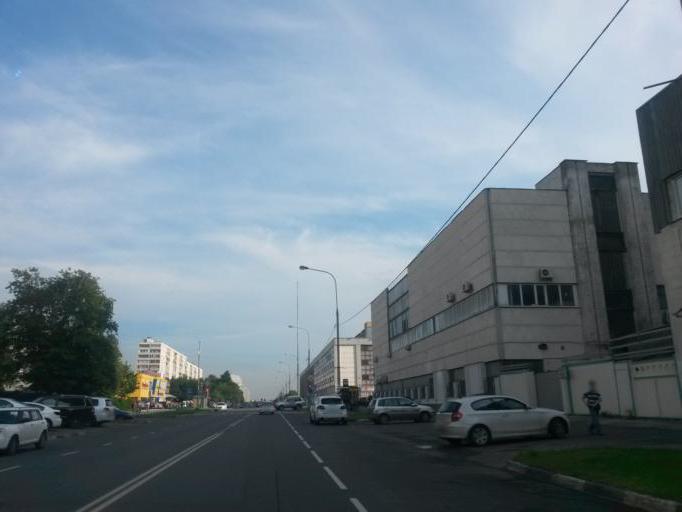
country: RU
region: Moscow
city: Orekhovo-Borisovo
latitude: 55.6164
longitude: 37.7194
